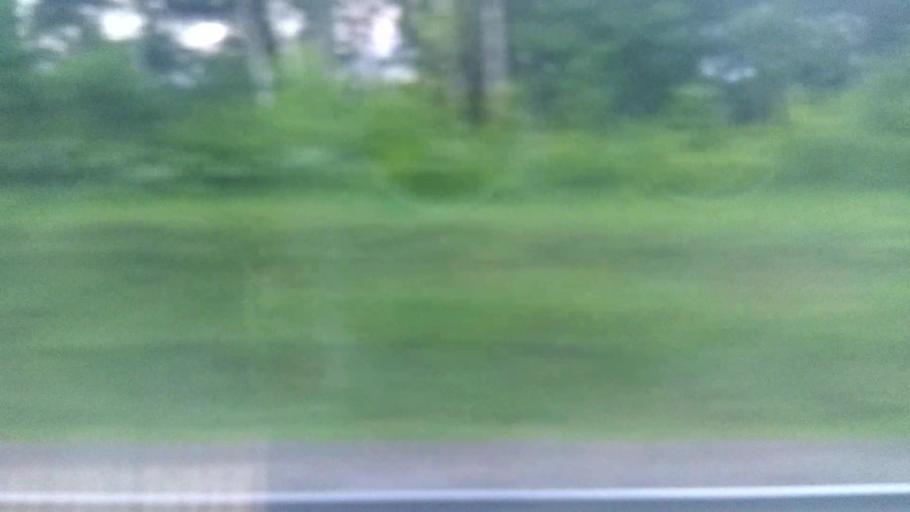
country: RU
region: Moskovskaya
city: Vidnoye
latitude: 55.5389
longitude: 37.6946
